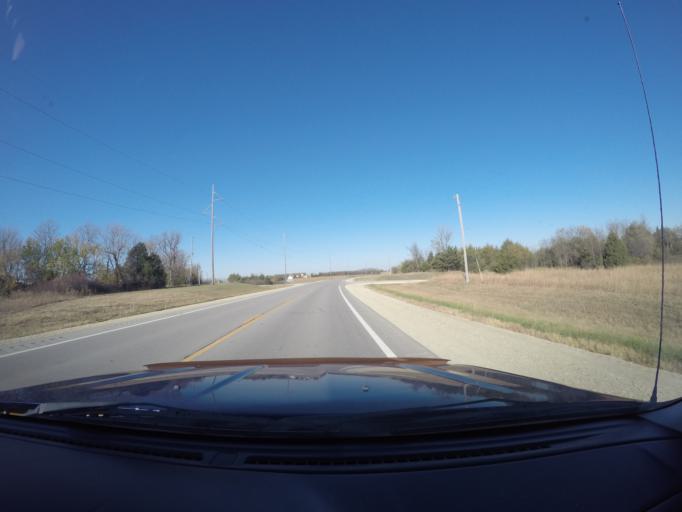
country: US
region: Kansas
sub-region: Riley County
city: Manhattan
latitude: 39.2539
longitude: -96.6718
